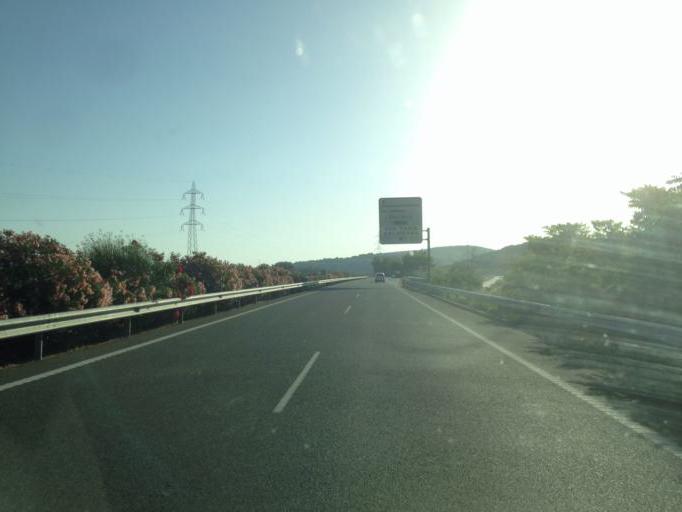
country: ES
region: Andalusia
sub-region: Provincia de Malaga
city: Villanueva de Tapia
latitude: 37.1152
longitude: -4.3017
